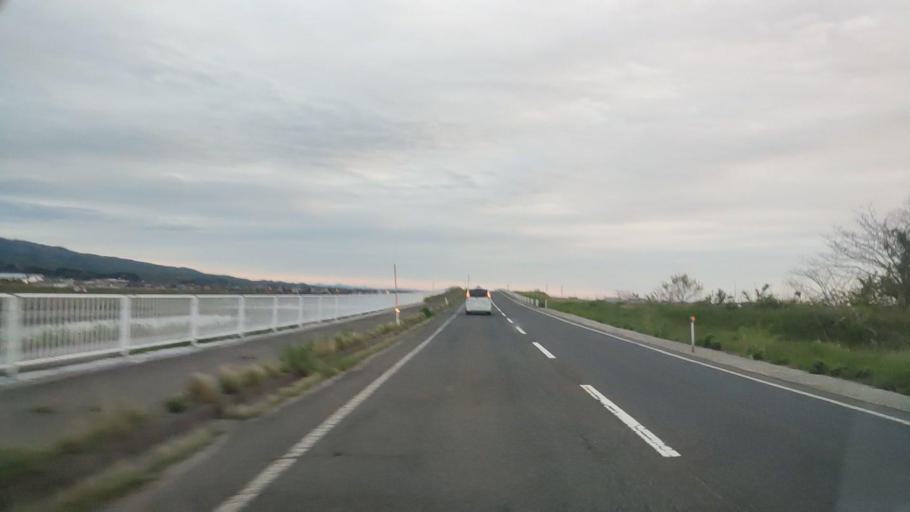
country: JP
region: Niigata
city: Niitsu-honcho
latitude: 37.7604
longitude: 139.0948
